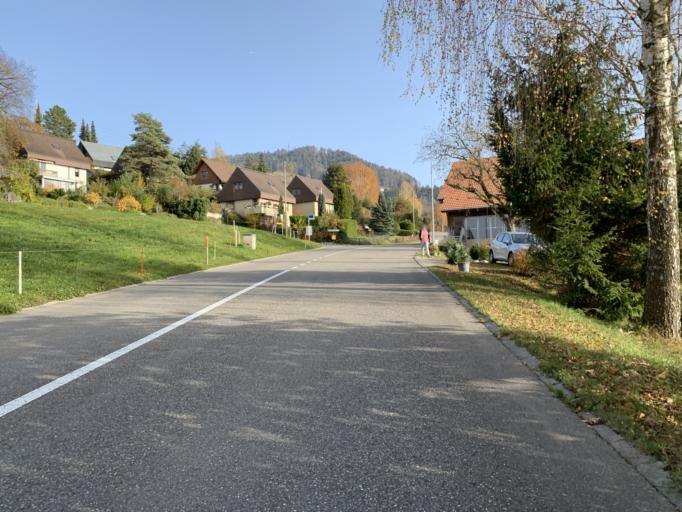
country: CH
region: Zurich
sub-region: Bezirk Hinwil
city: Hadlikon
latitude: 47.2973
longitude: 8.8605
